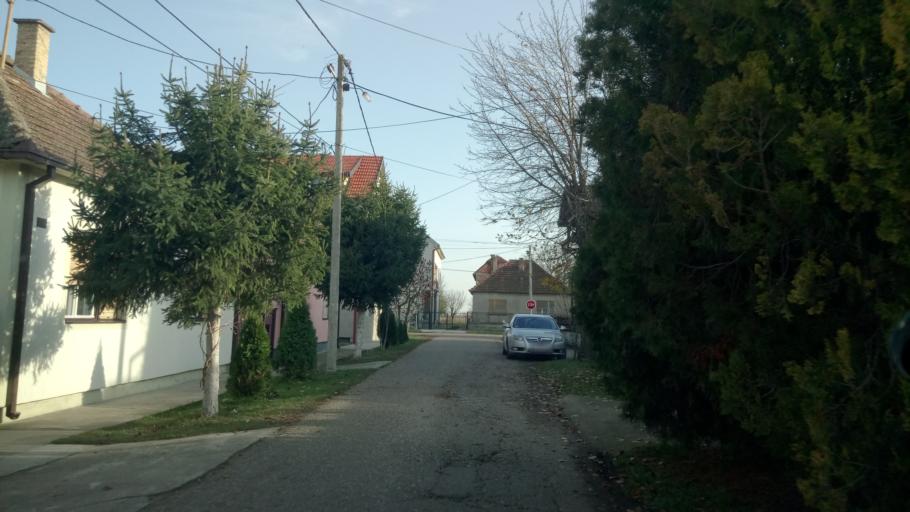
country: RS
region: Autonomna Pokrajina Vojvodina
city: Nova Pazova
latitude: 44.9475
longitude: 20.2345
